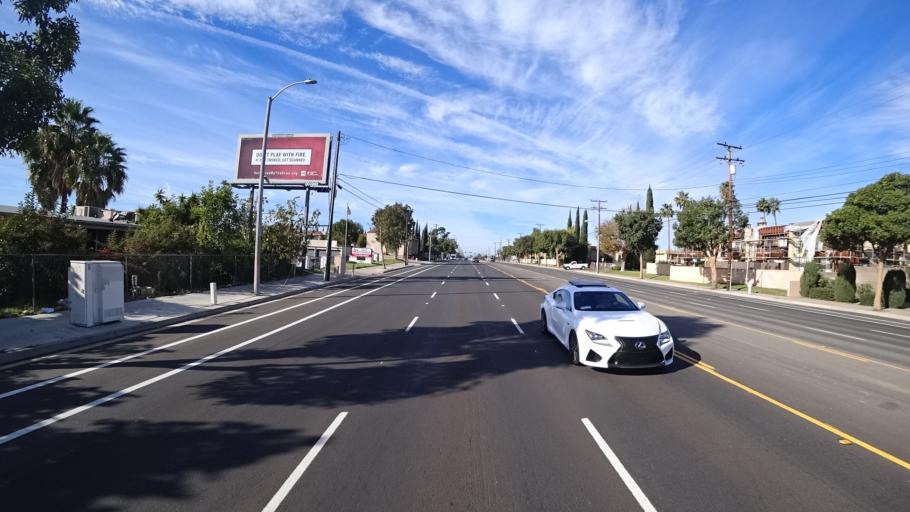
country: US
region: California
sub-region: Orange County
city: Garden Grove
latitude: 33.7450
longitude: -117.9341
